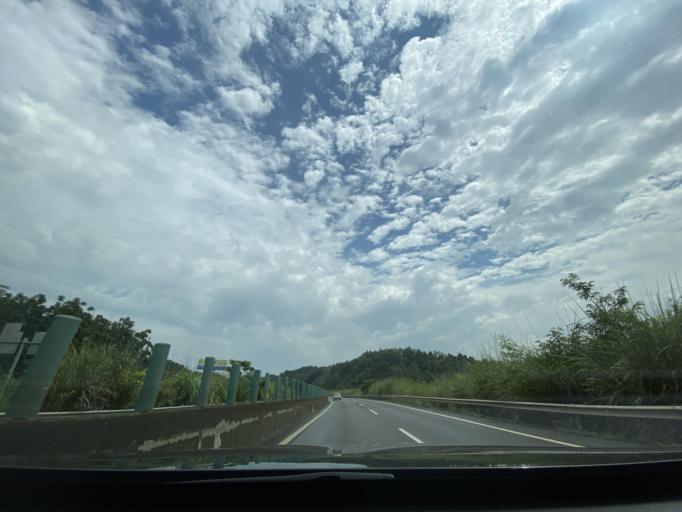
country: CN
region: Sichuan
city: Jiancheng
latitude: 30.2816
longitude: 104.5899
